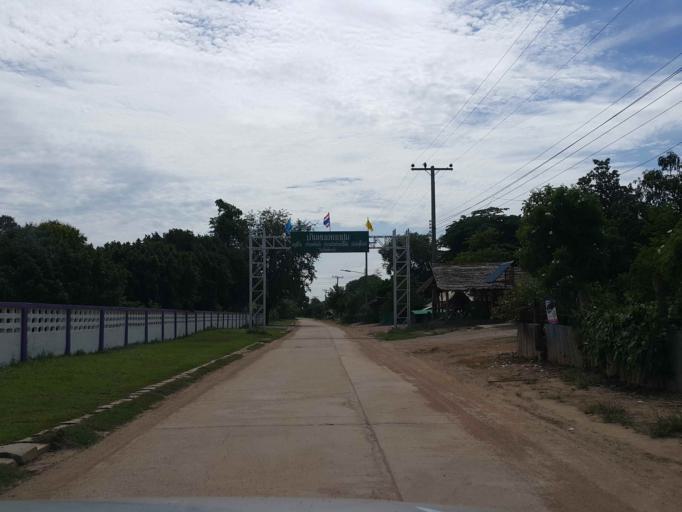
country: TH
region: Sukhothai
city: Ban Dan Lan Hoi
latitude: 17.1037
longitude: 99.4756
